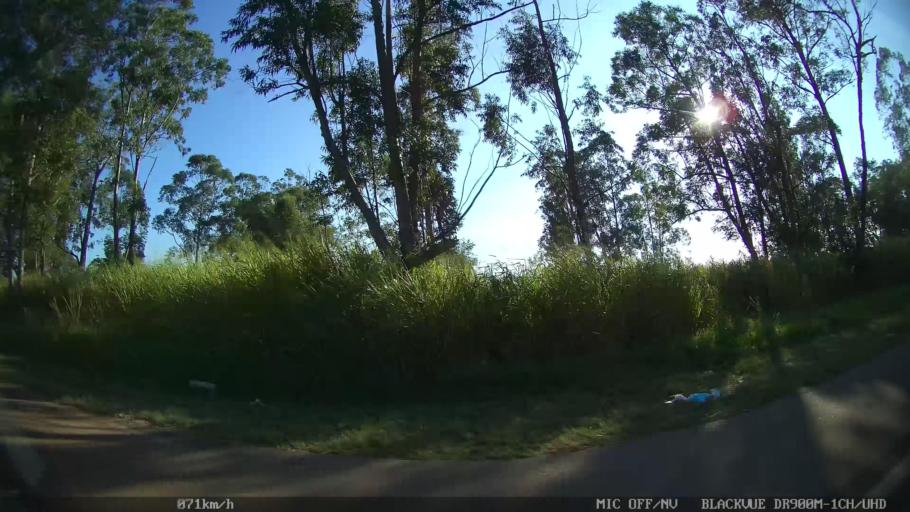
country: BR
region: Sao Paulo
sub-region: Itupeva
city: Itupeva
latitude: -23.0499
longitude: -47.0810
